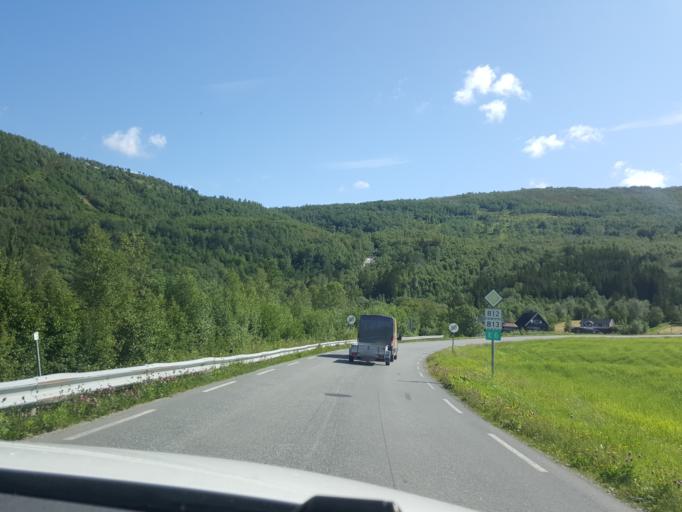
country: NO
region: Nordland
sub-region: Bodo
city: Loding
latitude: 67.1202
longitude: 15.0138
